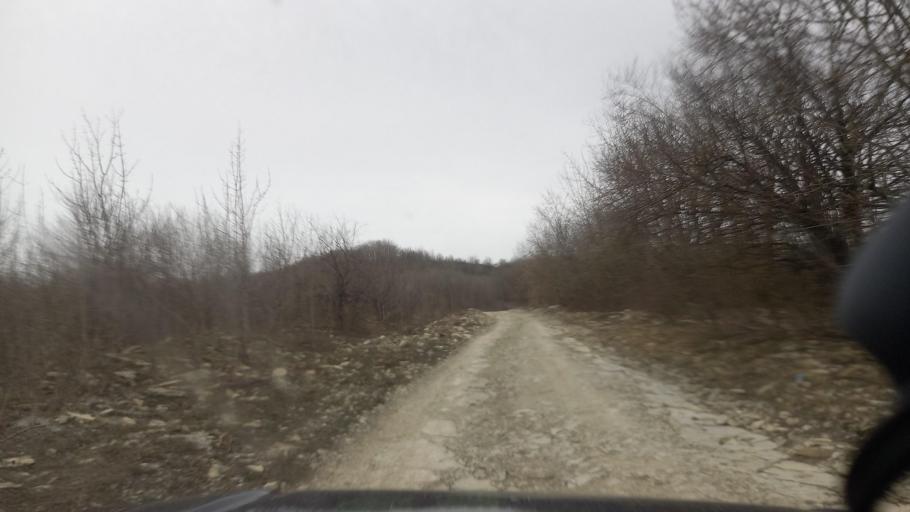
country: RU
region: Krasnodarskiy
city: Divnomorskoye
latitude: 44.6032
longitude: 38.2786
